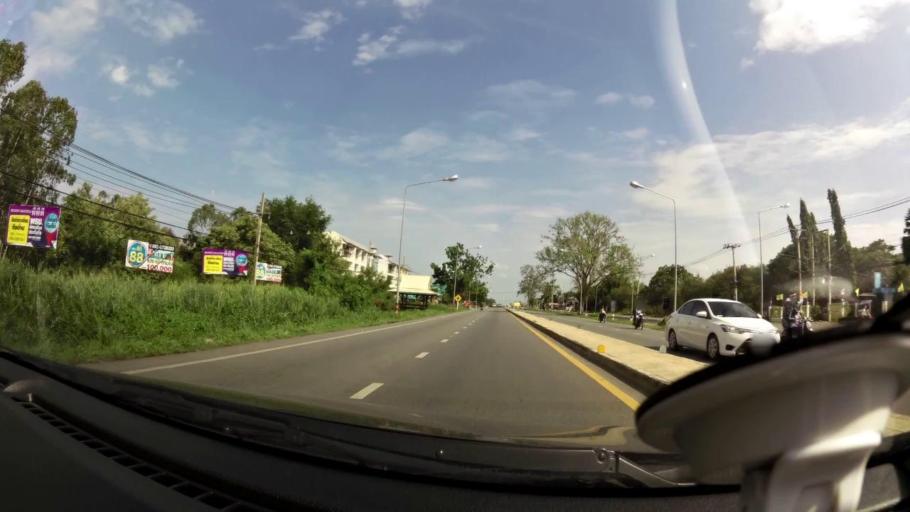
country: TH
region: Prachuap Khiri Khan
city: Hua Hin
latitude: 12.5263
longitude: 99.9625
